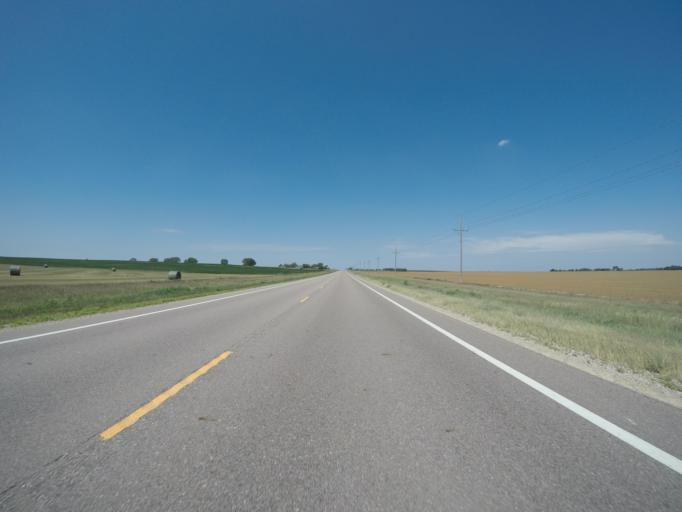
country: US
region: Kansas
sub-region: Osborne County
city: Osborne
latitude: 39.5098
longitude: -98.6404
